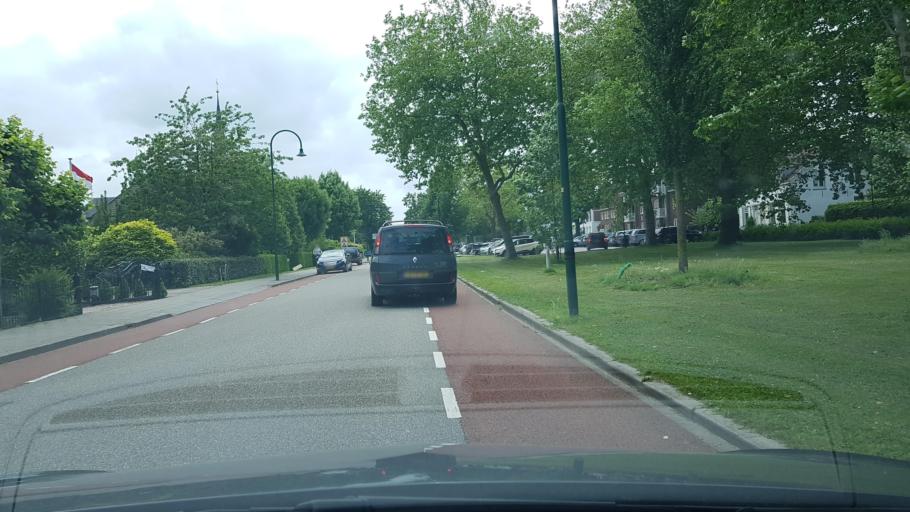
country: NL
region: Utrecht
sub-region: Stichtse Vecht
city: Vreeland
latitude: 52.2666
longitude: 5.0460
